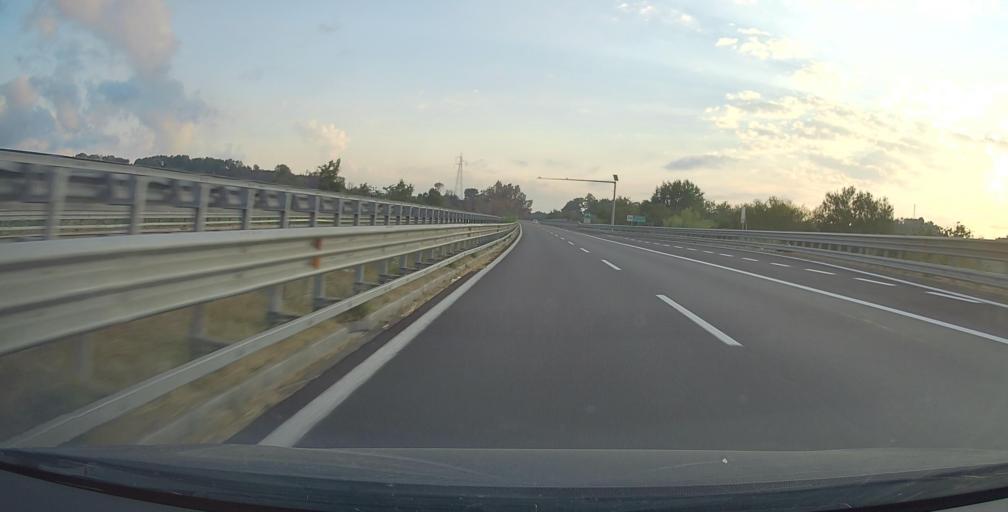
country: IT
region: Calabria
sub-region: Provincia di Reggio Calabria
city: Rosarno
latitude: 38.4903
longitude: 16.0094
